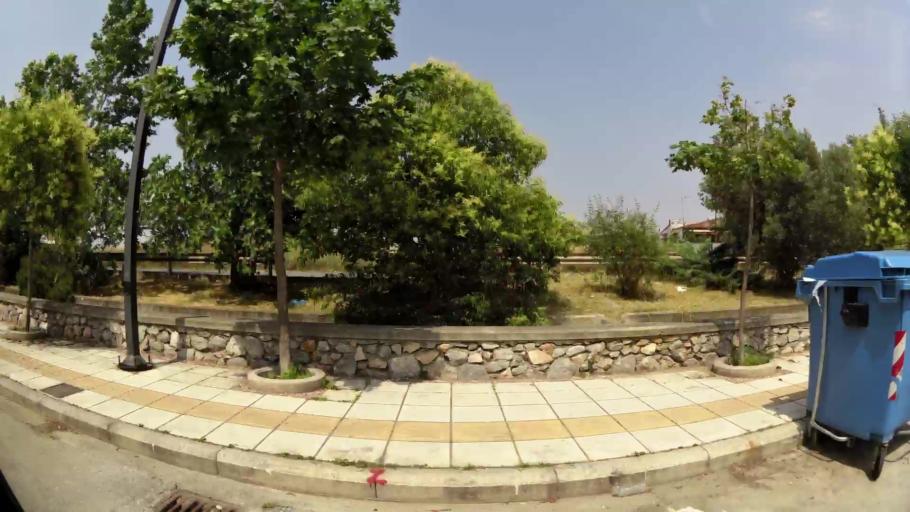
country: GR
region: Central Macedonia
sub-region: Nomos Thessalonikis
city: Diavata
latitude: 40.6882
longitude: 22.8622
